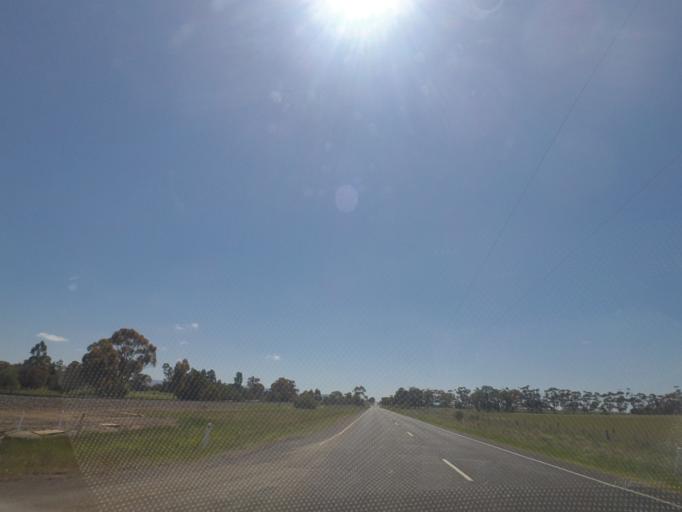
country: AU
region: Victoria
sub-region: Hume
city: Sunbury
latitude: -37.4940
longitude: 144.7581
